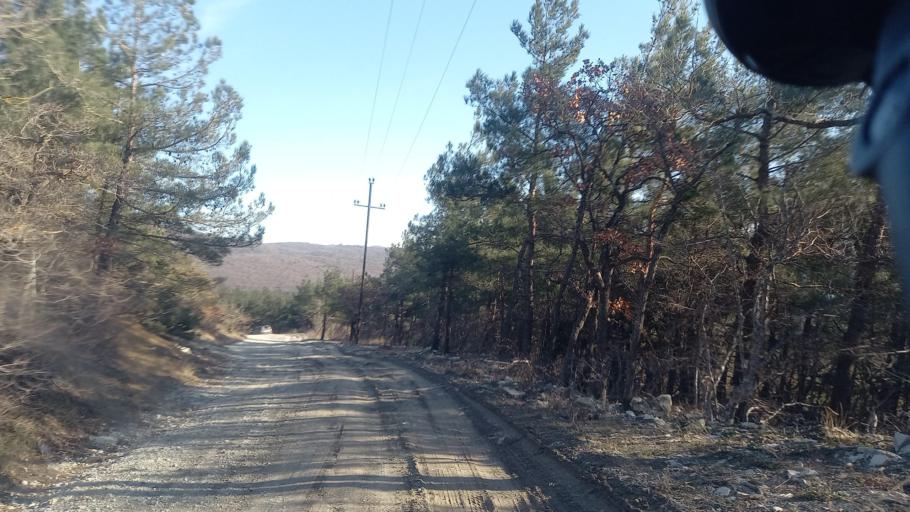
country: RU
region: Krasnodarskiy
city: Kabardinka
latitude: 44.6188
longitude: 37.9337
